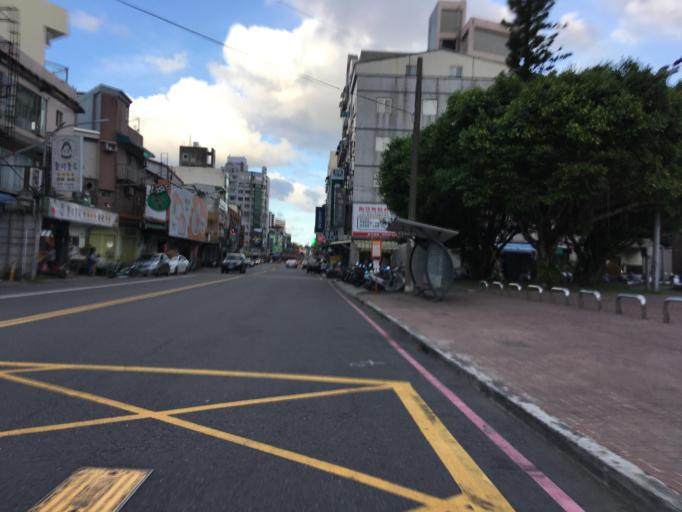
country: TW
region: Taiwan
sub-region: Yilan
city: Yilan
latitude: 24.6729
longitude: 121.7648
